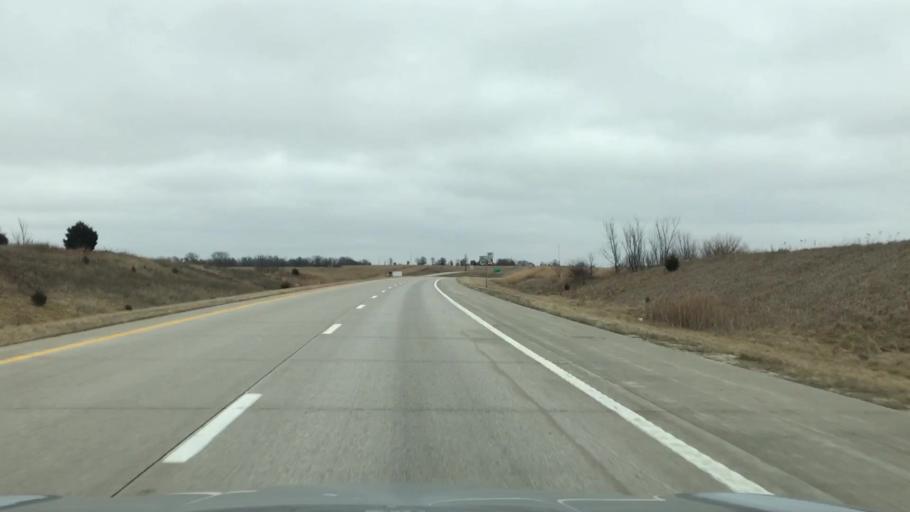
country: US
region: Missouri
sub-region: Linn County
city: Marceline
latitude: 39.7639
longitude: -92.7905
